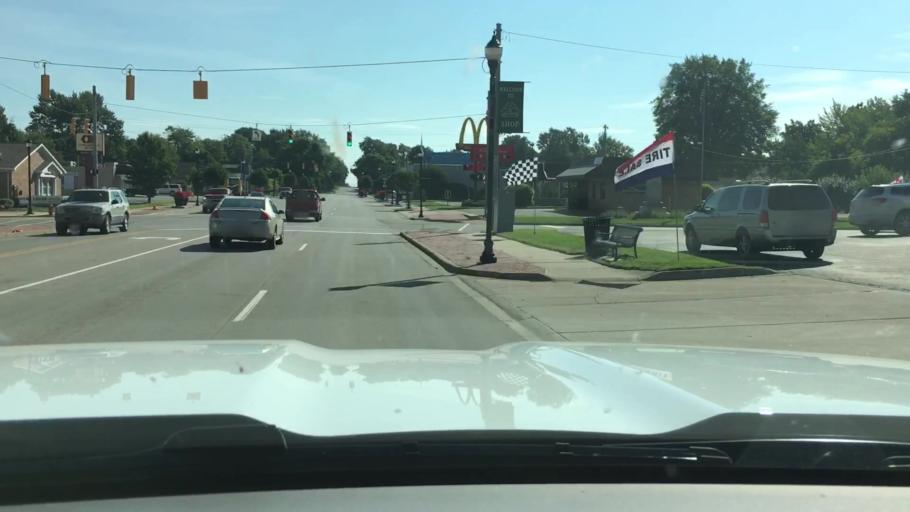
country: US
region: Michigan
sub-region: Gratiot County
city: Saint Louis
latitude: 43.4079
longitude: -84.6094
